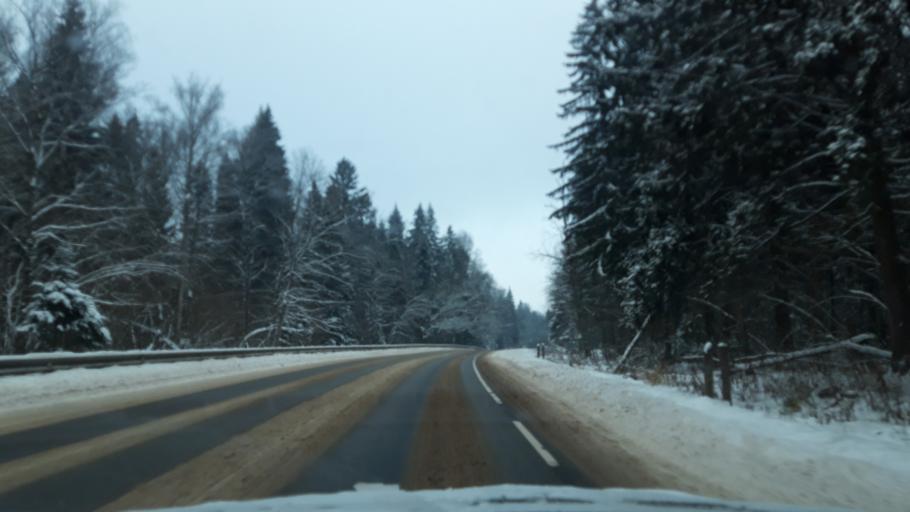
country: RU
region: Moskovskaya
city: Avtopoligon
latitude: 56.2863
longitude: 37.3814
